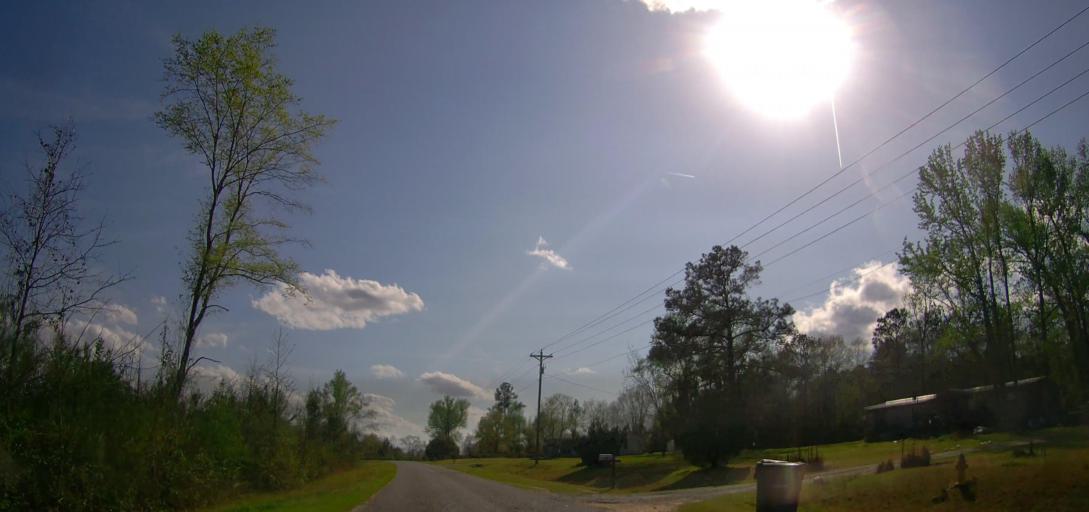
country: US
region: Georgia
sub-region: Baldwin County
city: Hardwick
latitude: 33.0364
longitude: -83.1178
